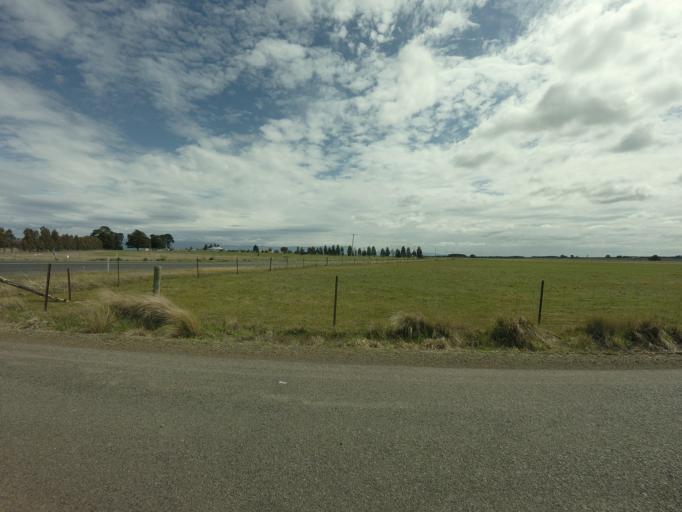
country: AU
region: Tasmania
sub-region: Northern Midlands
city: Longford
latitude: -41.7028
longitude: 147.1964
